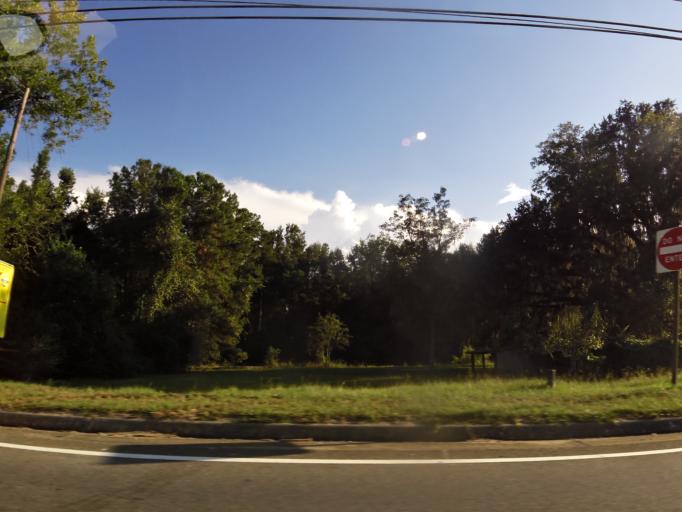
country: US
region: Georgia
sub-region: Brooks County
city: Quitman
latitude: 30.7843
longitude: -83.5443
